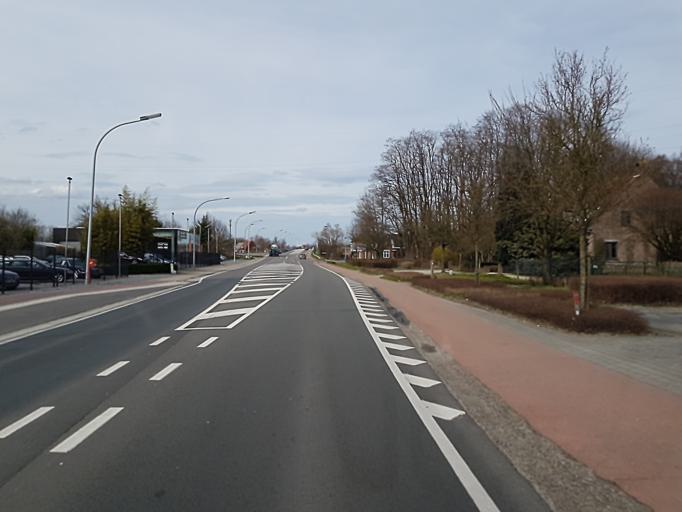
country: BE
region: Flanders
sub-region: Provincie Antwerpen
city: Dessel
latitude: 51.2205
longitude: 5.1151
